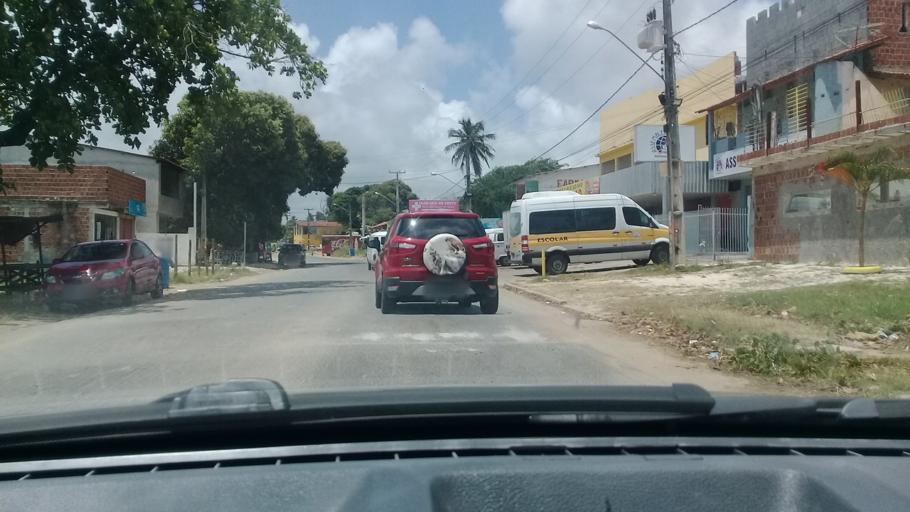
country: BR
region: Pernambuco
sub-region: Itamaraca
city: Itamaraca
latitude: -7.7863
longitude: -34.8400
